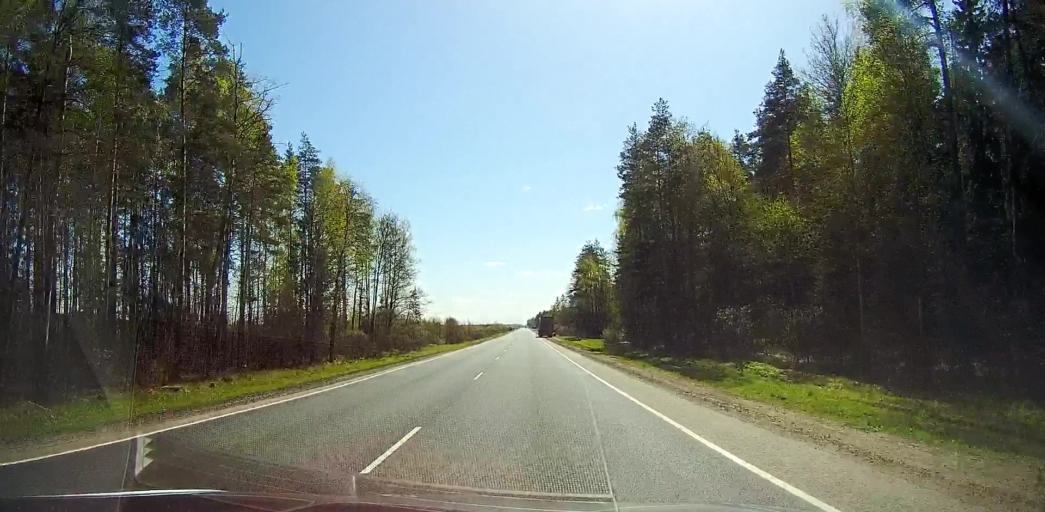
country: RU
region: Moskovskaya
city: Gzhel'
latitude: 55.6002
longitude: 38.3787
